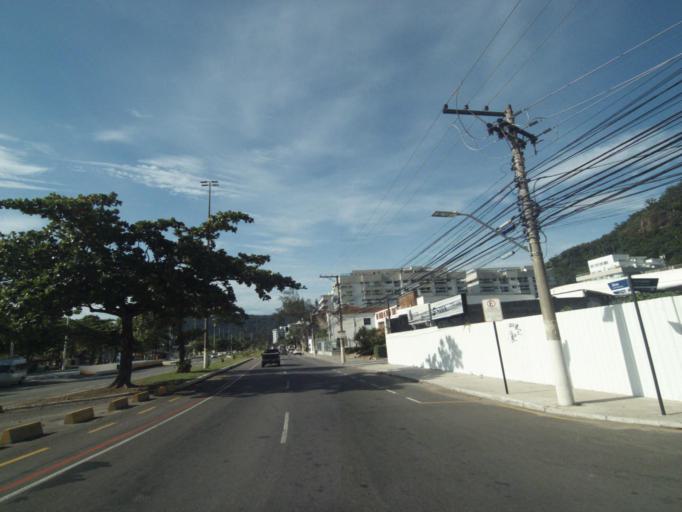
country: BR
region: Rio de Janeiro
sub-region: Niteroi
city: Niteroi
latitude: -22.9284
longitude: -43.0962
